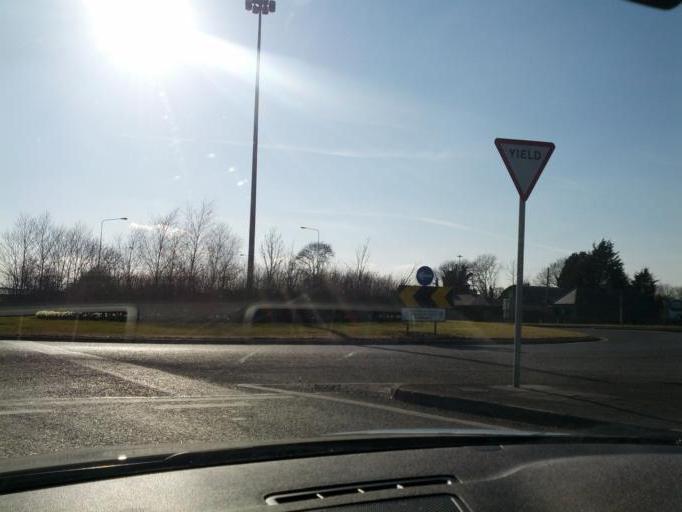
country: IE
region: Leinster
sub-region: Kildare
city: Naas
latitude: 53.2114
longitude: -6.7033
